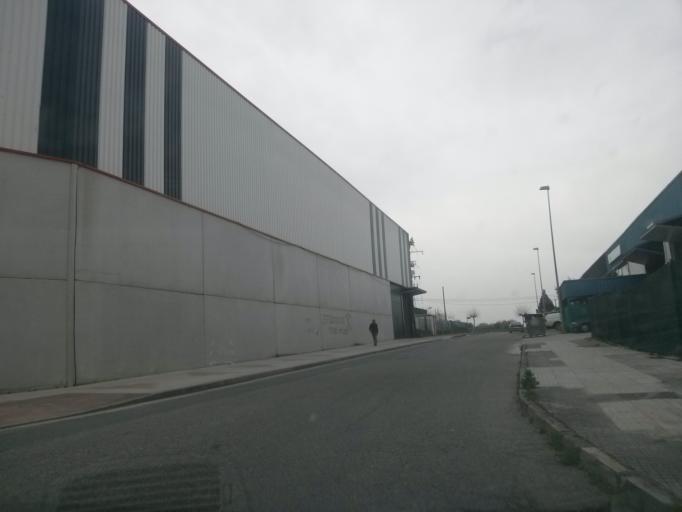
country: ES
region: Galicia
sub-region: Provincia de Lugo
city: Lugo
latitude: 43.0479
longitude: -7.5742
